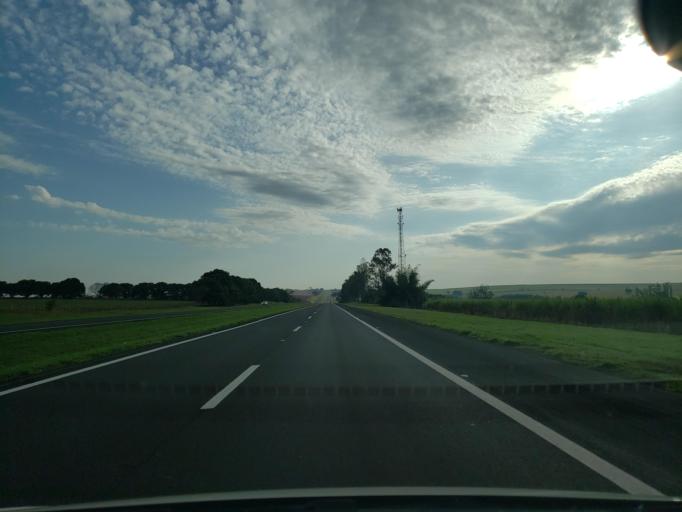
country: BR
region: Sao Paulo
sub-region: Valparaiso
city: Valparaiso
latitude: -21.2067
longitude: -50.7619
